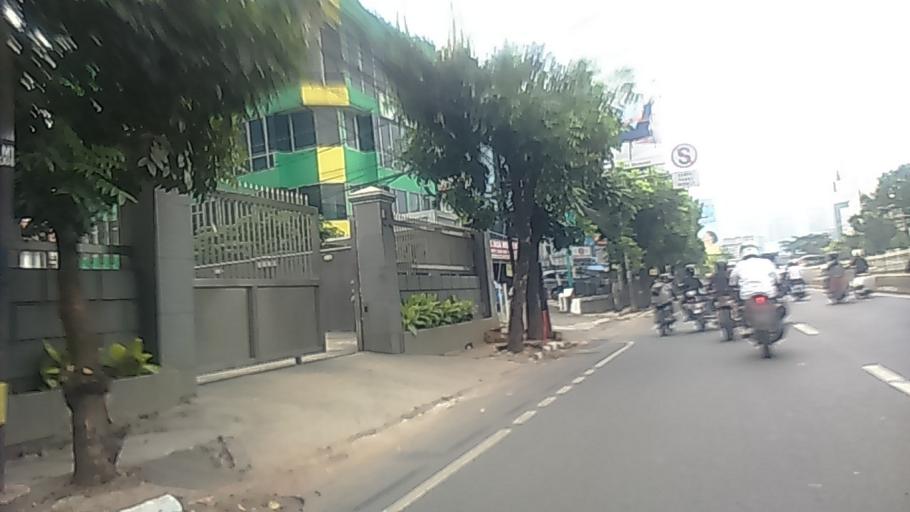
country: ID
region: Jakarta Raya
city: Jakarta
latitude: -6.2459
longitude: 106.8260
